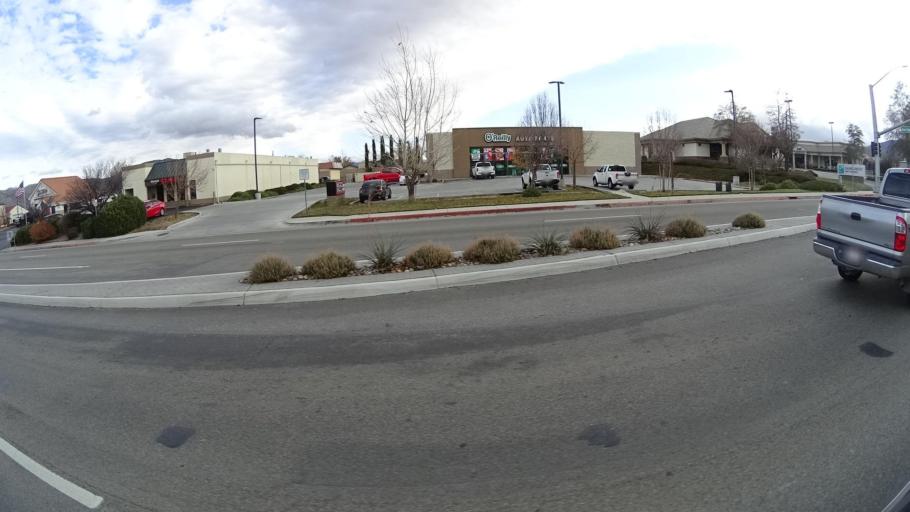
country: US
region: California
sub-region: Kern County
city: Tehachapi
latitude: 35.1266
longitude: -118.4679
